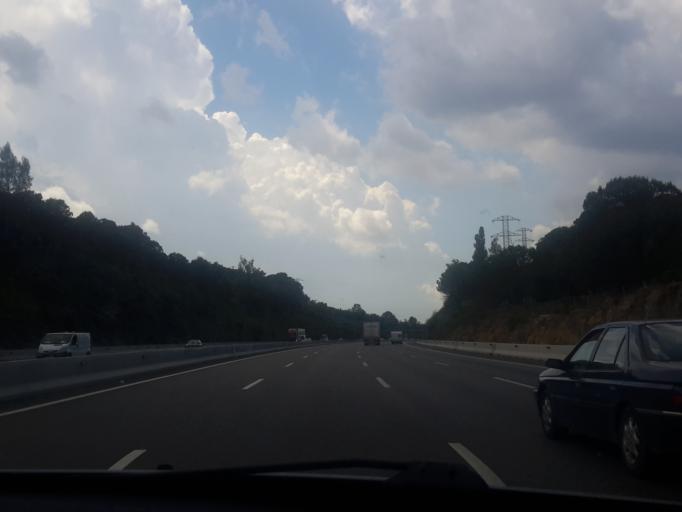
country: ES
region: Catalonia
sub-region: Provincia de Girona
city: Sarria de Ter
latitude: 42.0057
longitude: 2.8072
